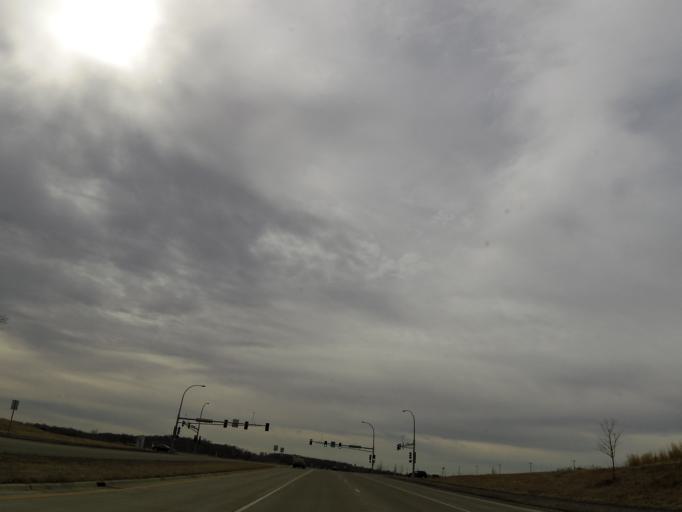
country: US
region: Minnesota
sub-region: Scott County
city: Prior Lake
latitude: 44.7686
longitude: -93.4355
